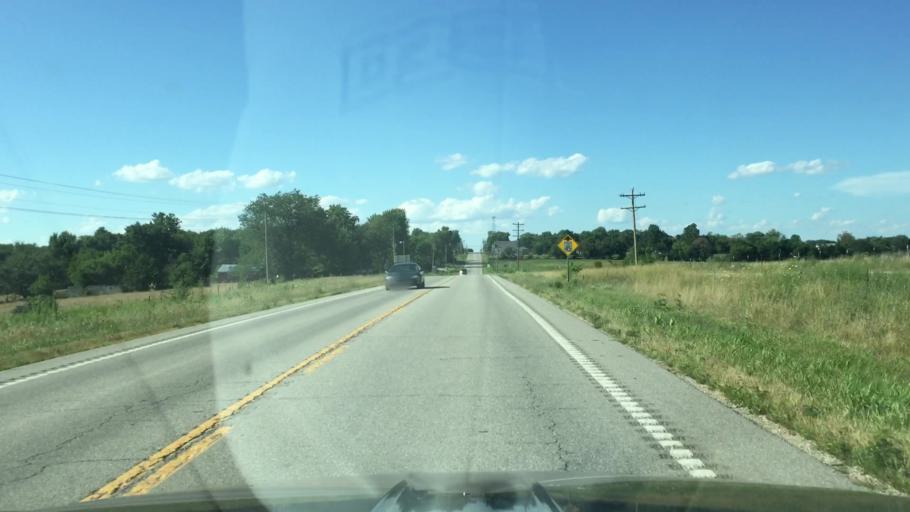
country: US
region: Missouri
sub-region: Moniteau County
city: Tipton
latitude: 38.5606
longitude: -92.7973
